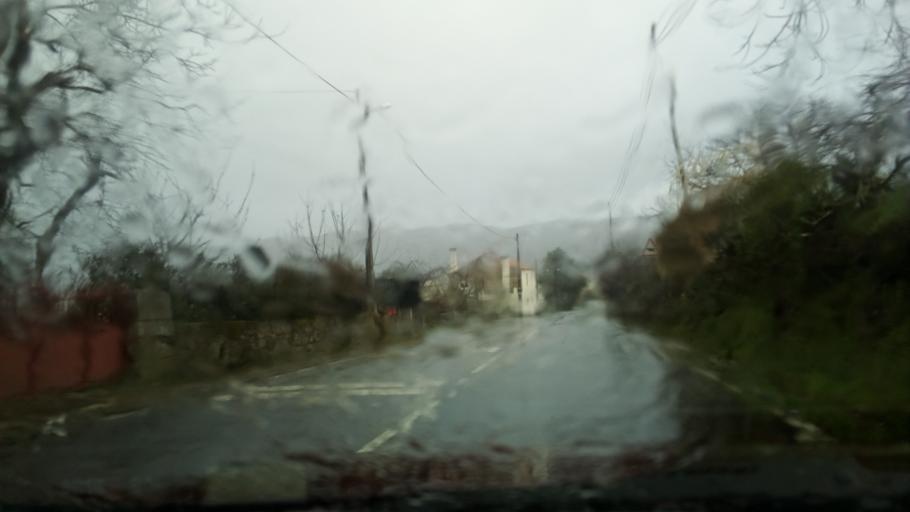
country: PT
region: Guarda
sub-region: Guarda
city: Guarda
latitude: 40.5435
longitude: -7.3210
